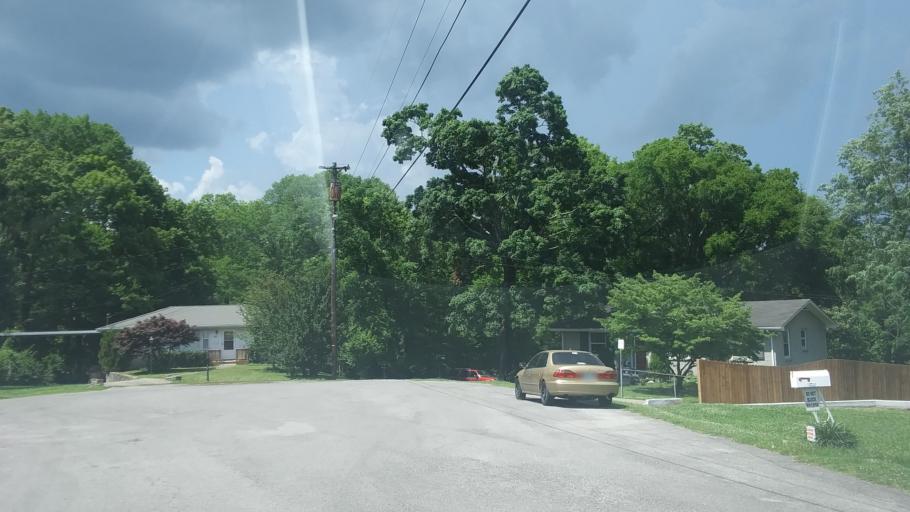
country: US
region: Tennessee
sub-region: Davidson County
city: Oak Hill
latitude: 36.0740
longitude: -86.7147
